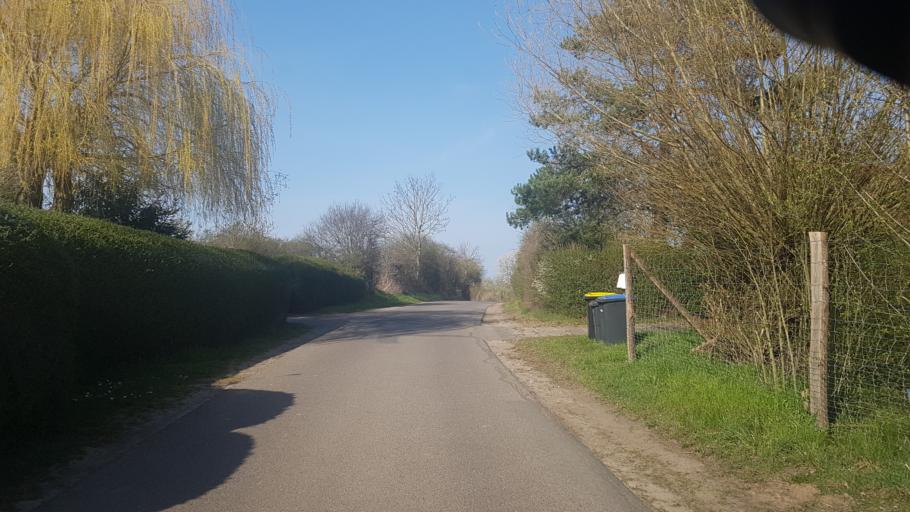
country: DE
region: Brandenburg
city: Gerswalde
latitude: 53.2066
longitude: 13.7830
